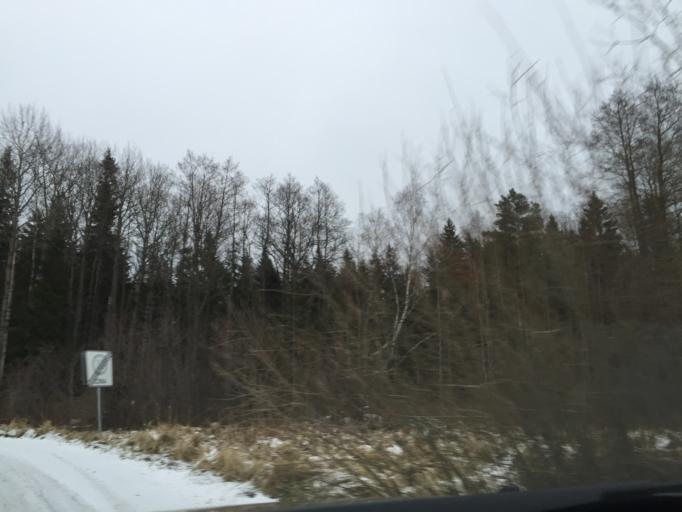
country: LV
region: Salacgrivas
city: Salacgriva
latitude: 57.5165
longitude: 24.3820
